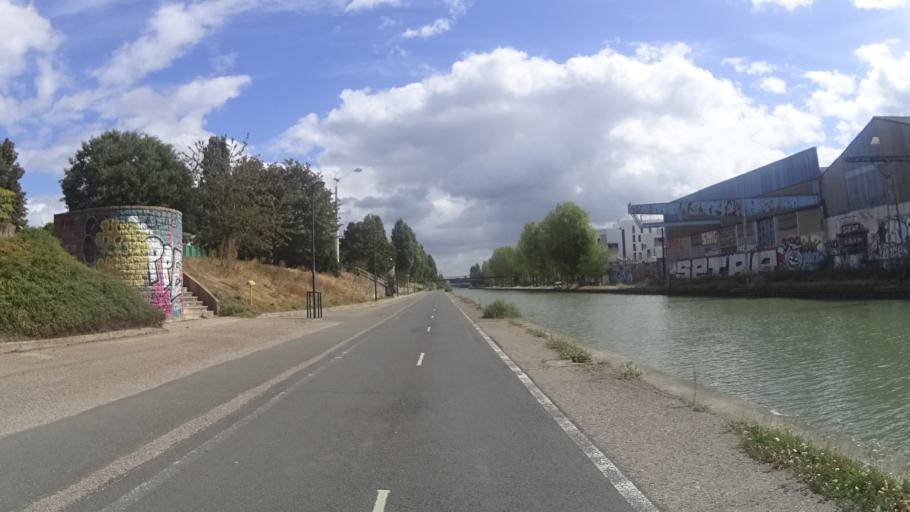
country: FR
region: Ile-de-France
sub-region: Departement de Seine-Saint-Denis
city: Bobigny
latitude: 48.9032
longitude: 2.4597
